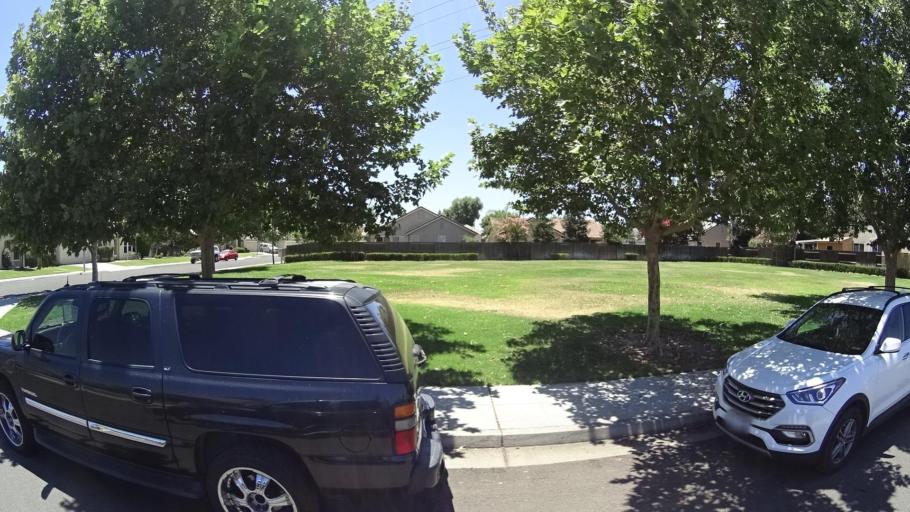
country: US
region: California
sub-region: Fresno County
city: Sunnyside
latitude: 36.7343
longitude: -119.6653
